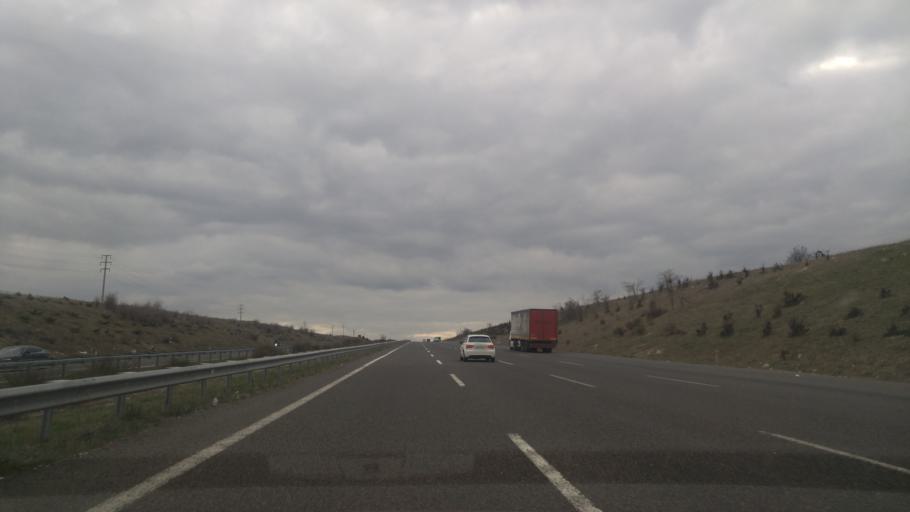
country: TR
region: Ankara
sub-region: Goelbasi
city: Golbasi
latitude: 39.7816
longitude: 32.6982
